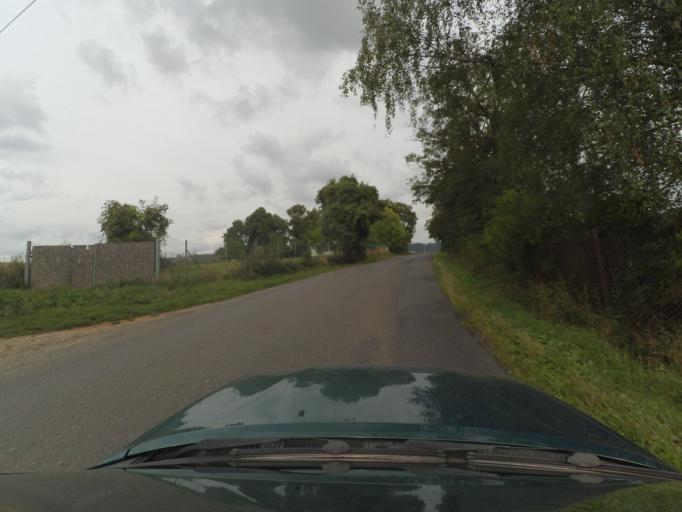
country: CZ
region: Central Bohemia
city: Revnicov
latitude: 50.1838
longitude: 13.7445
